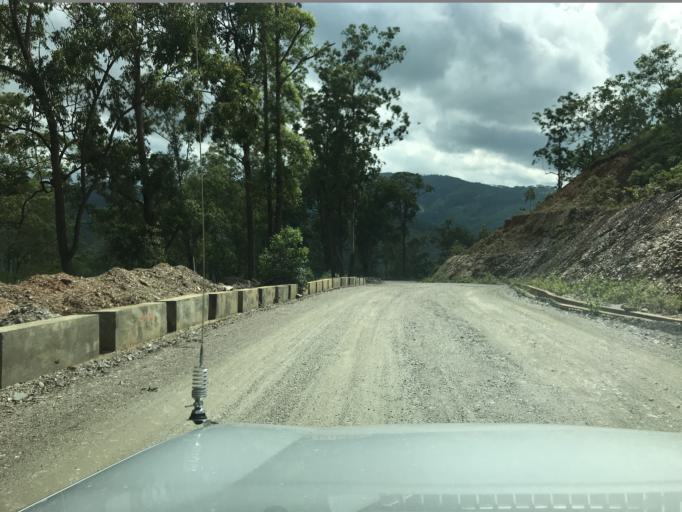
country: TL
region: Aileu
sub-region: Aileu Villa
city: Aileu
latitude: -8.6631
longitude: 125.5417
